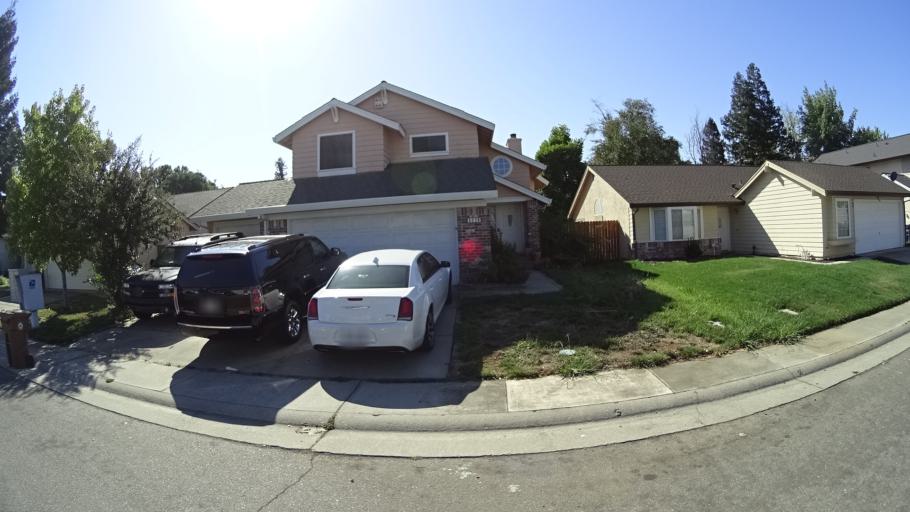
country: US
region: California
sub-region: Sacramento County
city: Laguna
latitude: 38.4369
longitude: -121.4434
